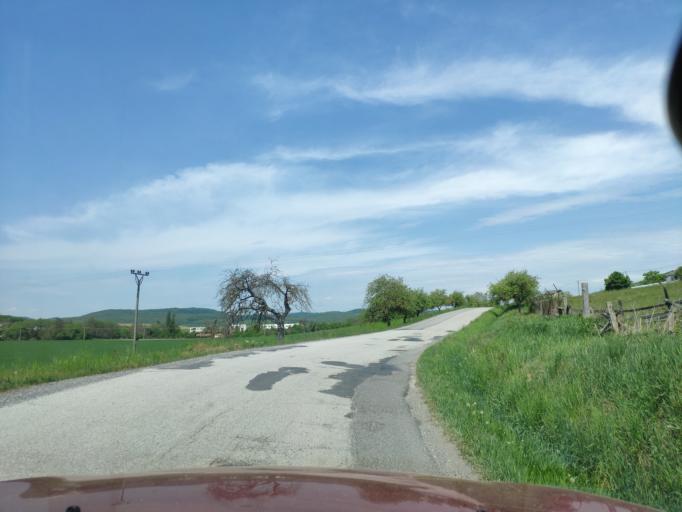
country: SK
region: Banskobystricky
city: Rimavska Sobota
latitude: 48.4655
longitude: 20.1018
